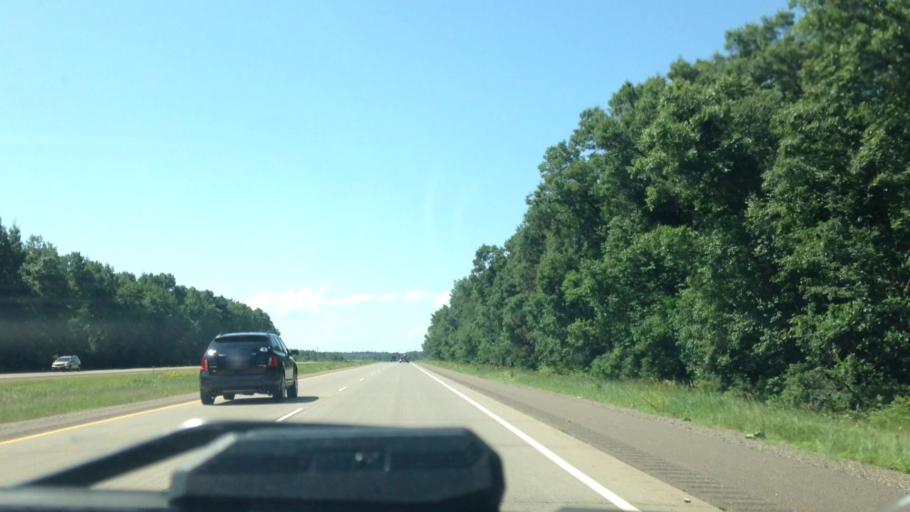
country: US
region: Wisconsin
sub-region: Barron County
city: Cameron
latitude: 45.4301
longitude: -91.7621
